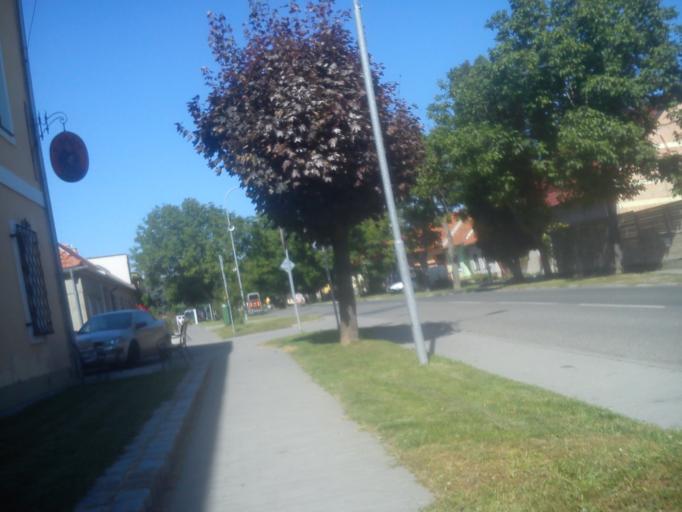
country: CZ
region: South Moravian
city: Sokolnice
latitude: 49.1018
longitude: 16.7548
